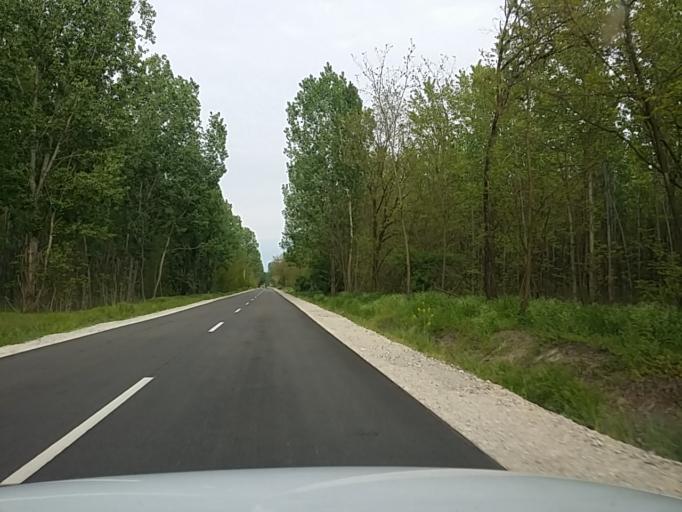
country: HU
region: Pest
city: Zsambok
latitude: 47.5576
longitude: 19.6589
